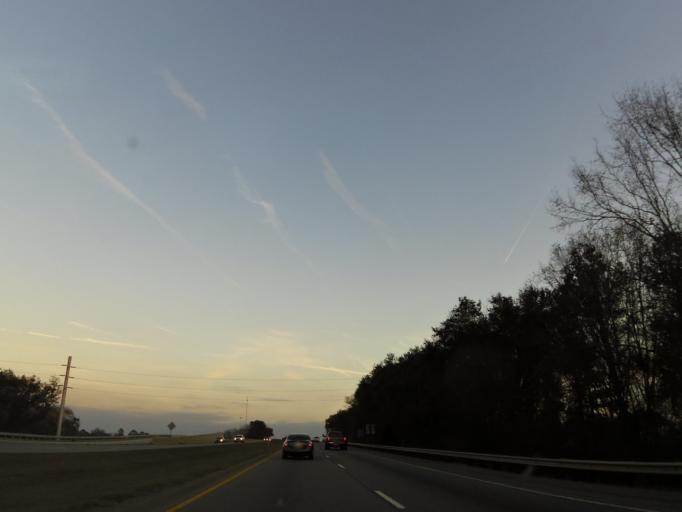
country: US
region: Georgia
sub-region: Dougherty County
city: Albany
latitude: 31.6101
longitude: -84.1600
